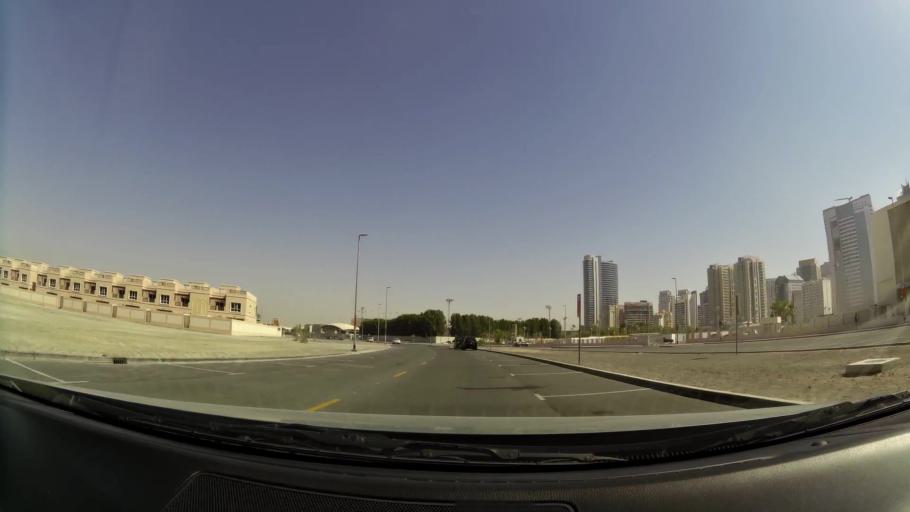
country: AE
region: Dubai
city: Dubai
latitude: 25.1041
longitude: 55.1822
